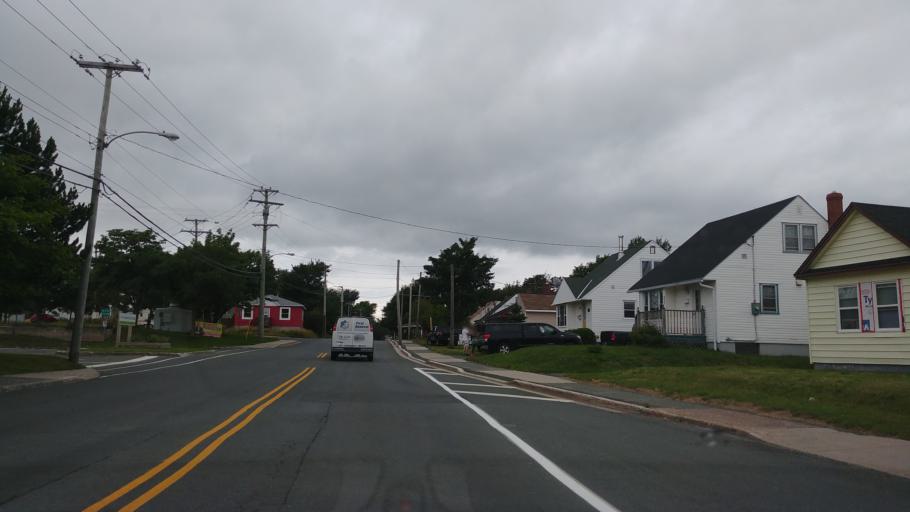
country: CA
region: Newfoundland and Labrador
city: St. John's
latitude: 47.5631
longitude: -52.7413
